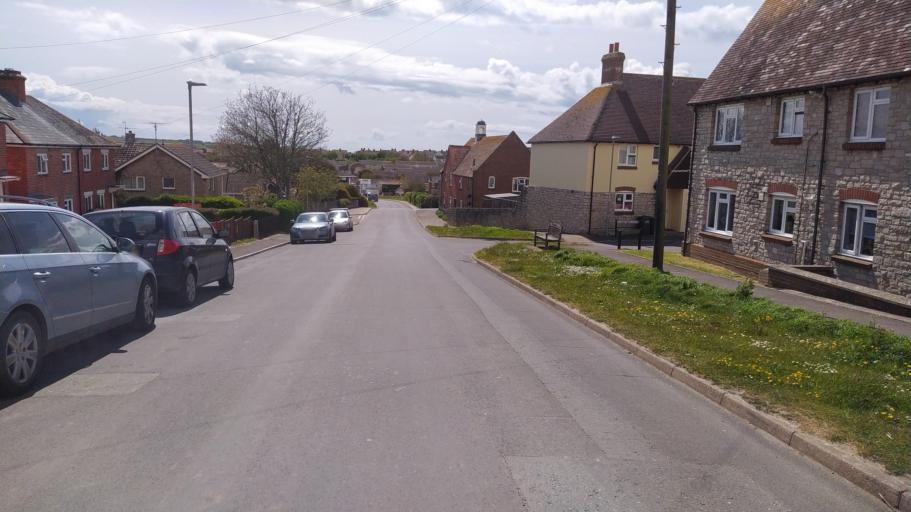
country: GB
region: England
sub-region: Dorset
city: Chickerell
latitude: 50.6256
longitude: -2.4987
